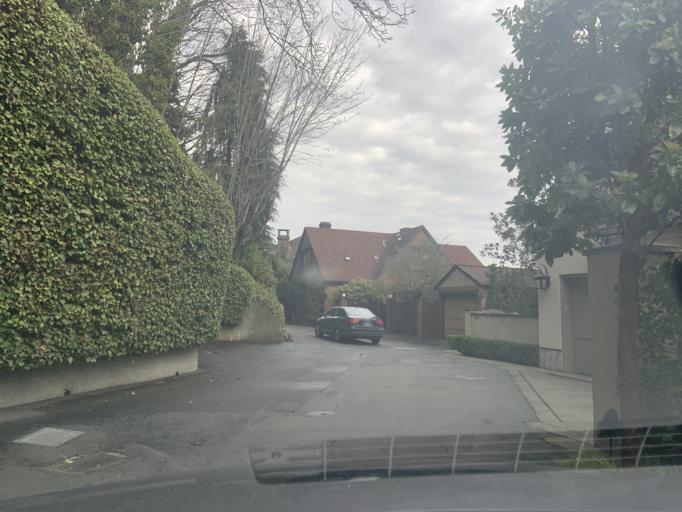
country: US
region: Washington
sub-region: King County
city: Medina
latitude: 47.6540
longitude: -122.2748
